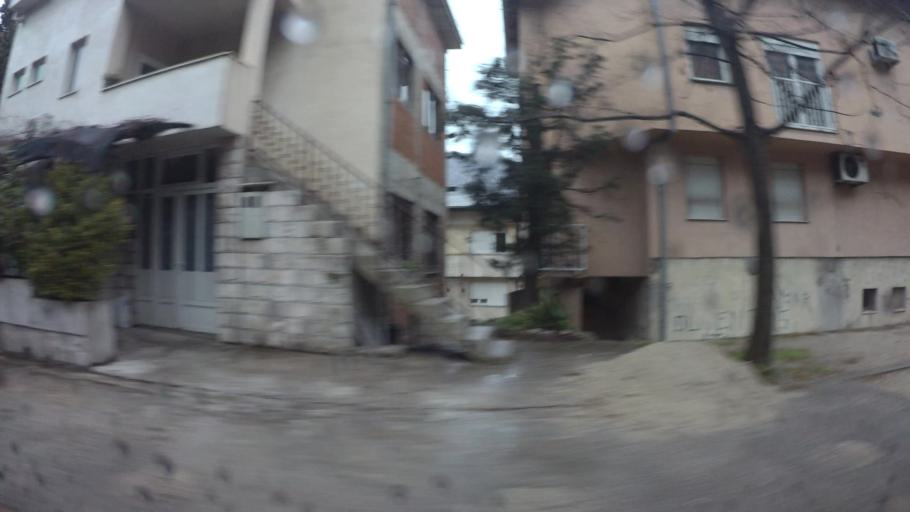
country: BA
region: Federation of Bosnia and Herzegovina
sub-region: Hercegovacko-Bosanski Kanton
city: Mostar
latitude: 43.3339
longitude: 17.8142
